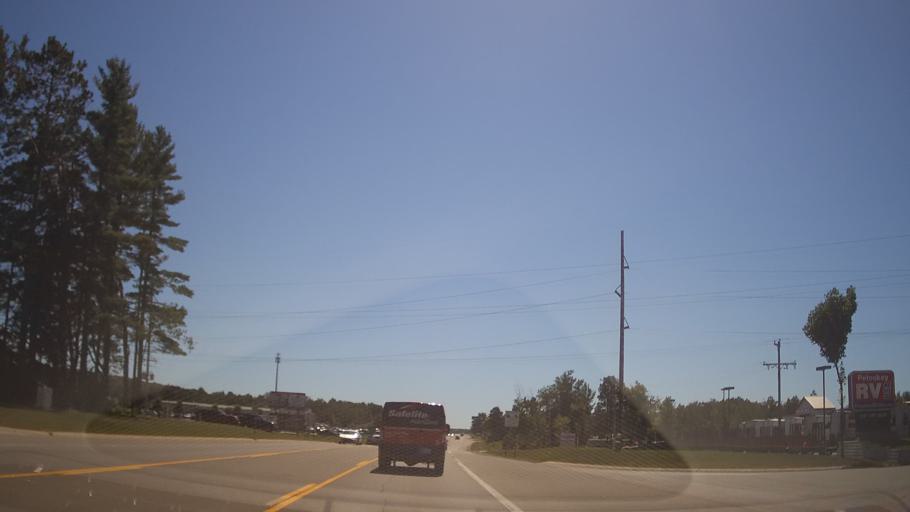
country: US
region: Michigan
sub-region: Emmet County
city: Petoskey
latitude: 45.4026
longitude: -84.8773
